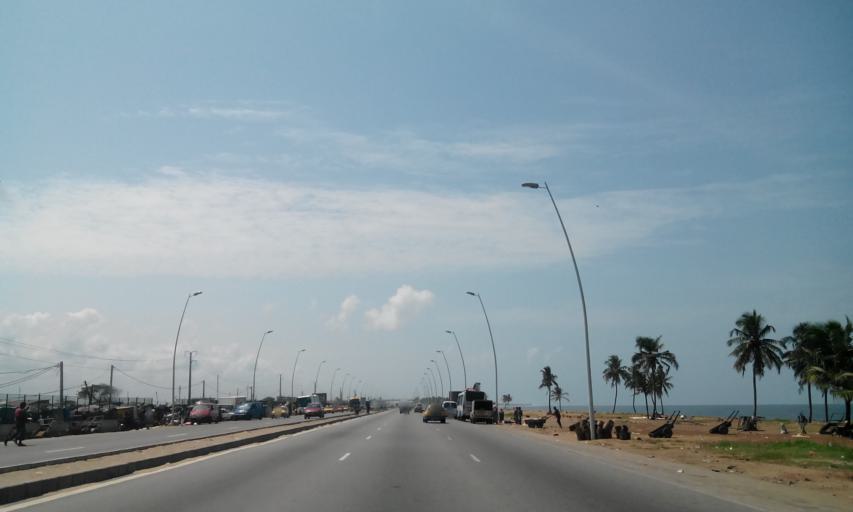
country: CI
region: Lagunes
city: Bingerville
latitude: 5.2413
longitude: -3.9092
